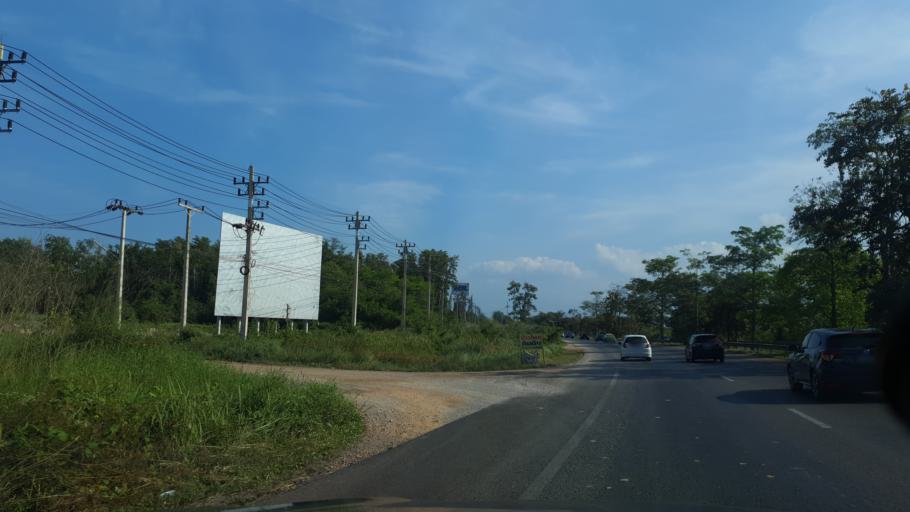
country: TH
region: Surat Thani
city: Phunphin
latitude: 9.0324
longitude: 99.1721
